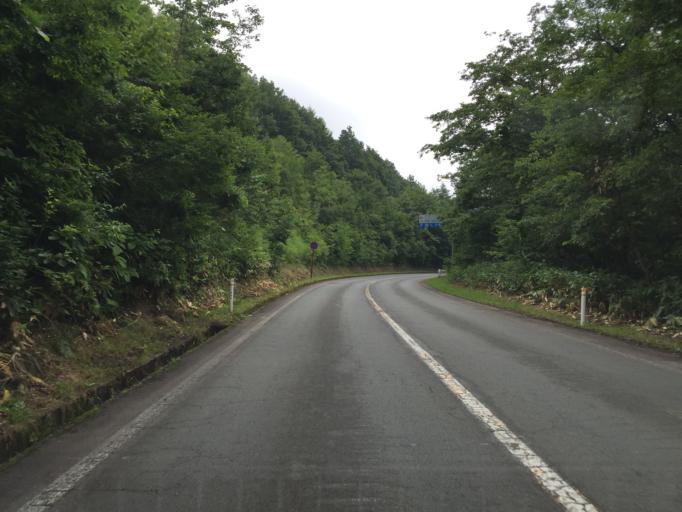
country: JP
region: Fukushima
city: Inawashiro
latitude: 37.6705
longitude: 140.1470
